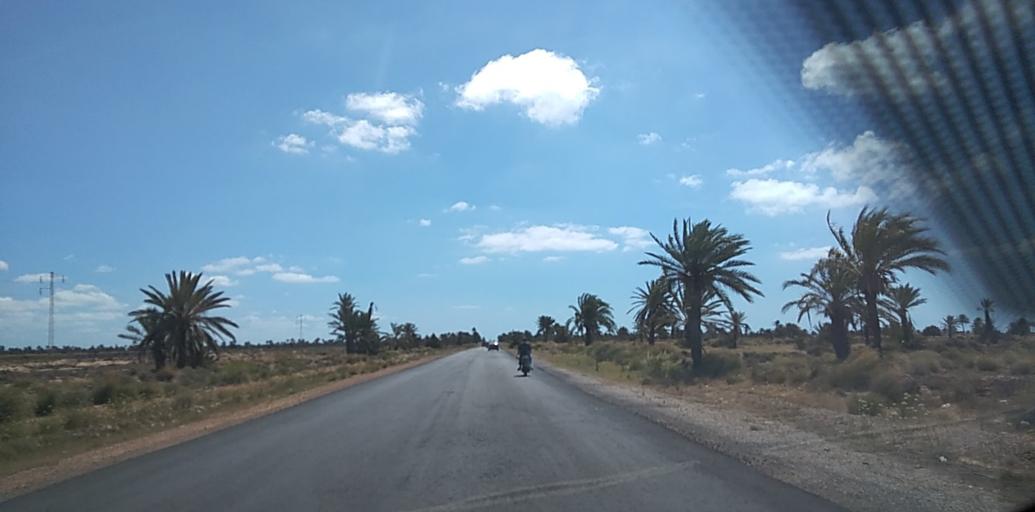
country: TN
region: Safaqis
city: Al Qarmadah
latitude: 34.6590
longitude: 11.1057
